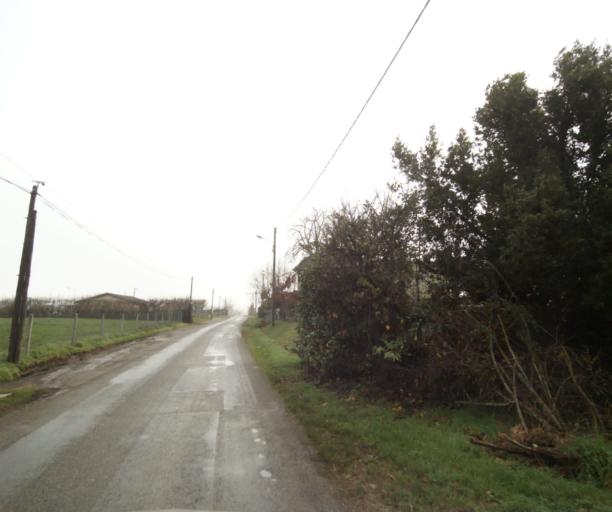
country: FR
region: Midi-Pyrenees
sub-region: Departement de la Haute-Garonne
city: Villaudric
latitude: 43.8375
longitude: 1.4624
